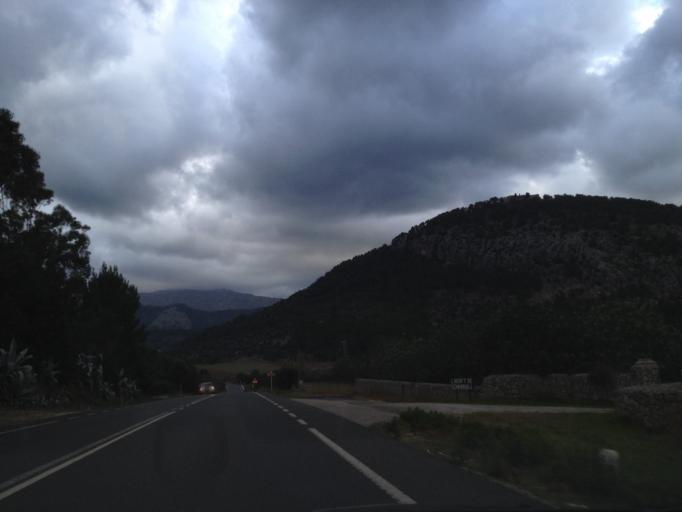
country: ES
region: Balearic Islands
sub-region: Illes Balears
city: Pollenca
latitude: 39.8582
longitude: 3.0279
